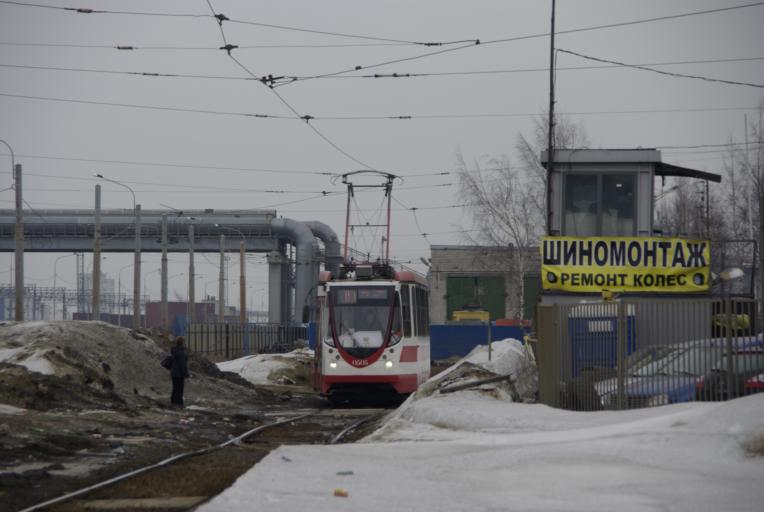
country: RU
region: Leningrad
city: Parnas
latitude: 60.0602
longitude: 30.3417
